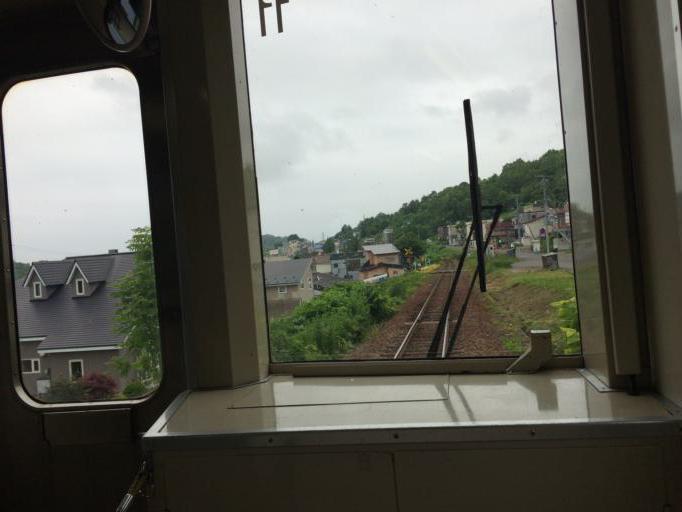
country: JP
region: Hokkaido
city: Otaru
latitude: 43.2090
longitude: 140.9675
